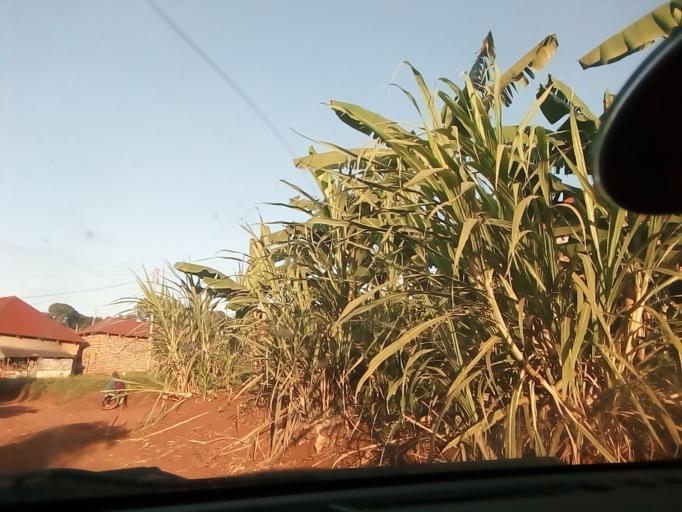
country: UG
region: Central Region
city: Masaka
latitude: -0.3397
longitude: 31.7583
